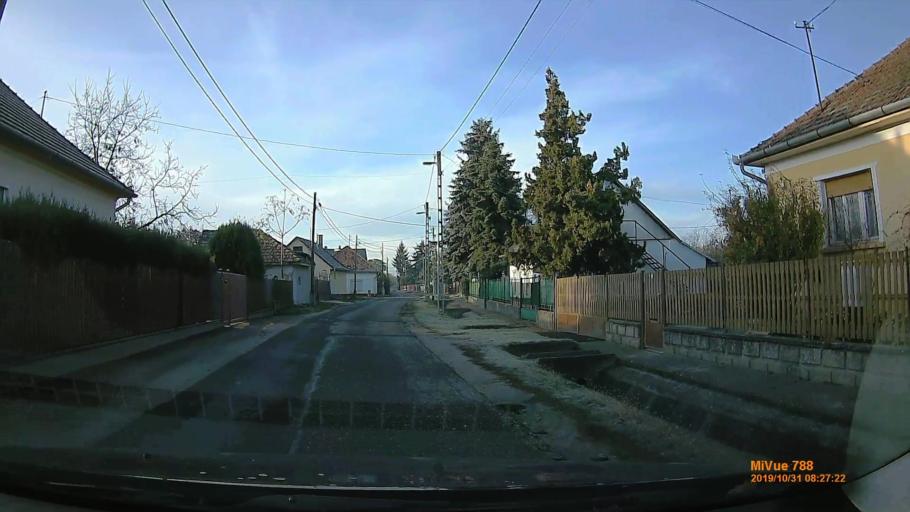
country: HU
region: Pest
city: Tapiobicske
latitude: 47.3625
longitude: 19.6828
